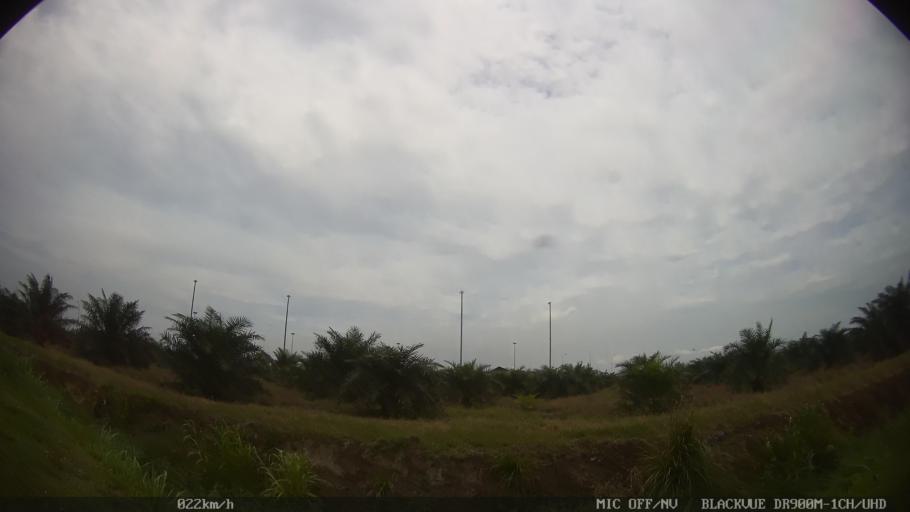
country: ID
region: North Sumatra
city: Sunggal
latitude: 3.6312
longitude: 98.5819
